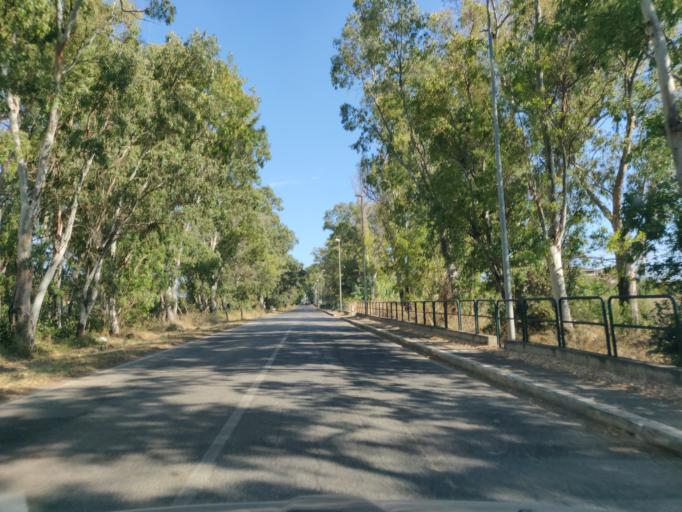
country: IT
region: Latium
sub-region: Citta metropolitana di Roma Capitale
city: Aurelia
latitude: 42.1482
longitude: 11.7606
